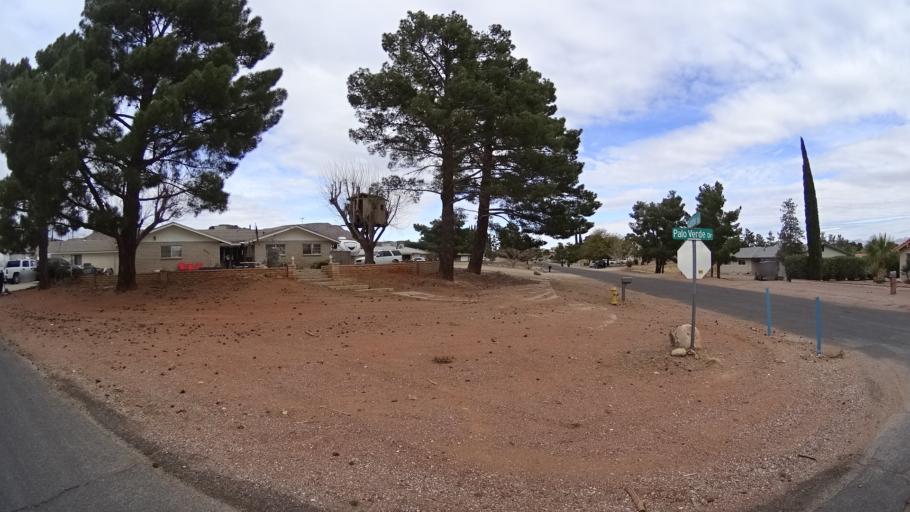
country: US
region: Arizona
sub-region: Mohave County
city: New Kingman-Butler
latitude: 35.2340
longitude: -114.0462
